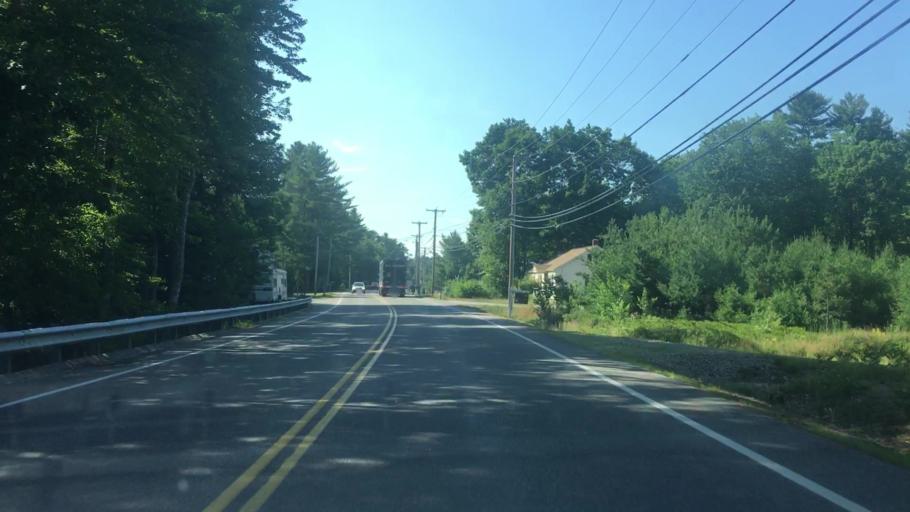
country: US
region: Maine
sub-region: York County
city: Biddeford
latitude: 43.5523
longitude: -70.4928
